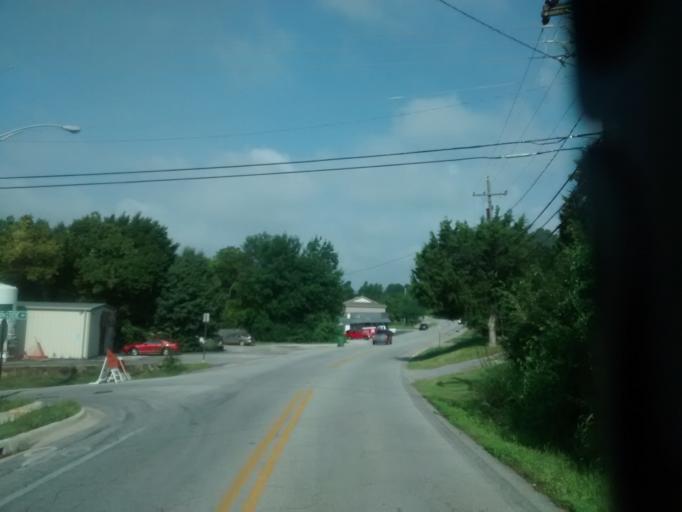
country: US
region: Arkansas
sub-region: Washington County
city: Fayetteville
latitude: 36.0553
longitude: -94.1487
